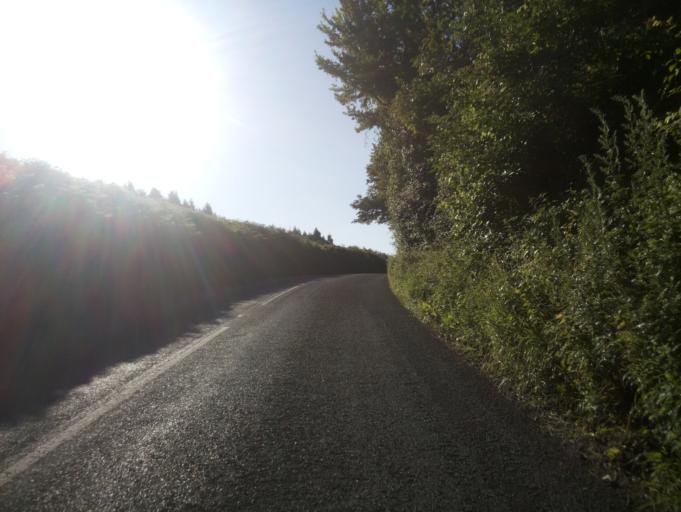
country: GB
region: Wales
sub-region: Monmouthshire
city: Chepstow
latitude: 51.6507
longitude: -2.7119
